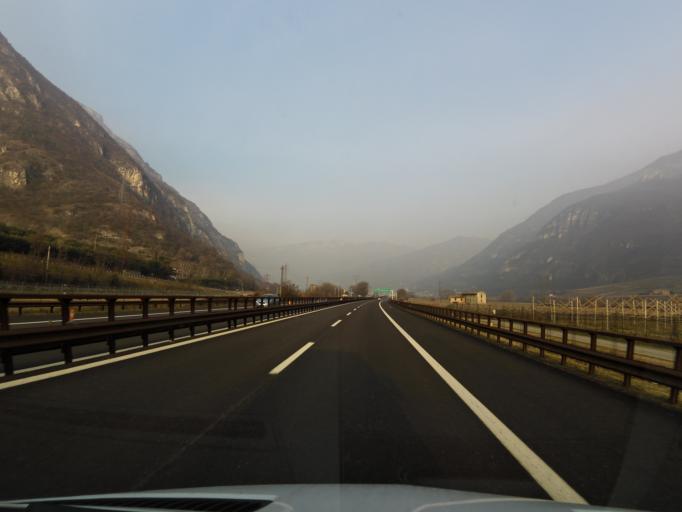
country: IT
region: Trentino-Alto Adige
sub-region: Provincia di Trento
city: Sabbionara
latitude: 45.7423
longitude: 10.9715
